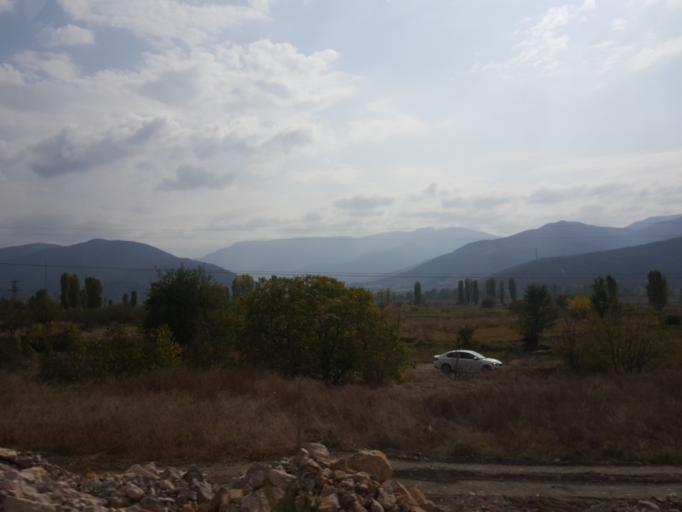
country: TR
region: Corum
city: Hacihamza
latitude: 41.1162
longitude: 34.4011
